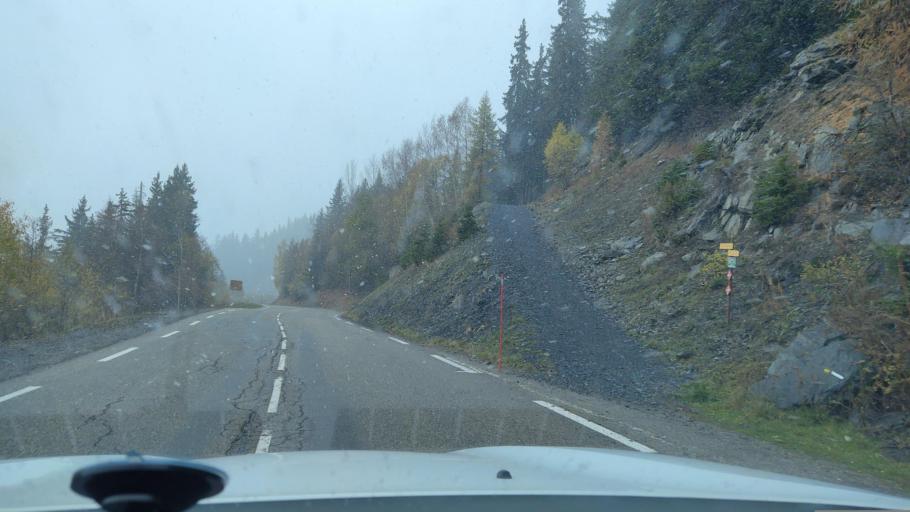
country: FR
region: Rhone-Alpes
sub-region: Departement de la Savoie
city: Bourg-Saint-Maurice
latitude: 45.5805
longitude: 6.7885
